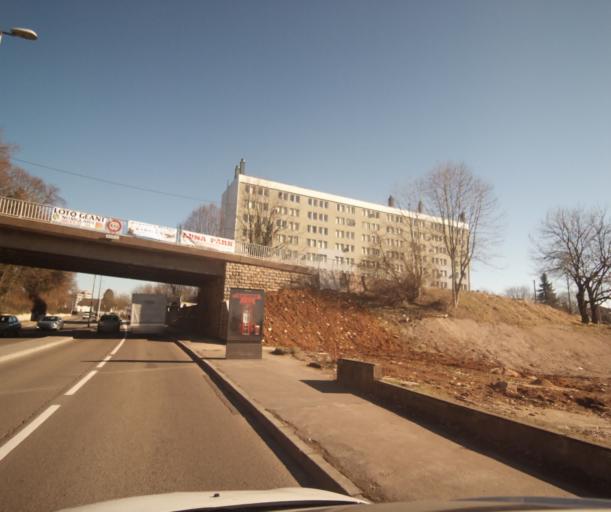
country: FR
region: Franche-Comte
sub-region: Departement du Doubs
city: Besancon
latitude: 47.2517
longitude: 6.0124
